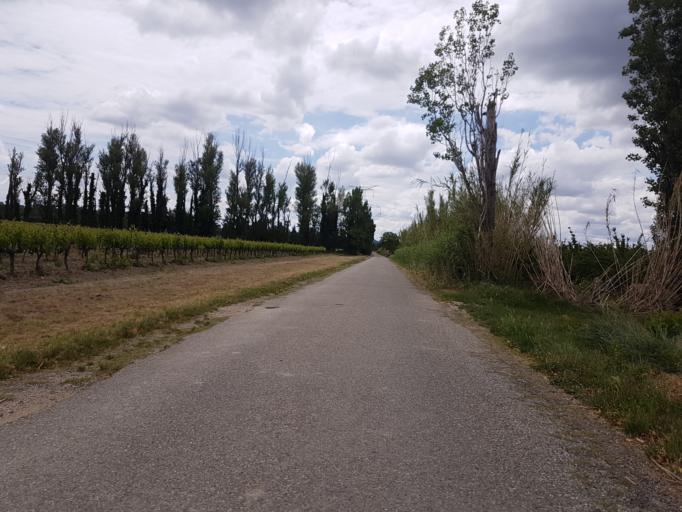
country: FR
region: Languedoc-Roussillon
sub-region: Departement du Gard
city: Vallabregues
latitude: 43.8788
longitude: 4.6279
